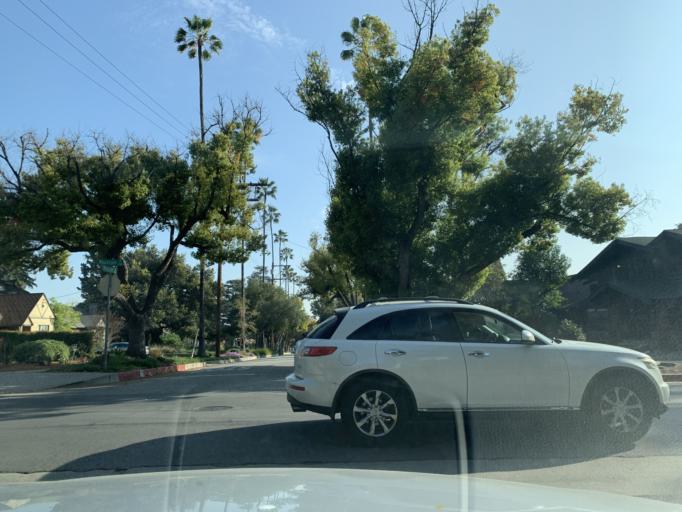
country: US
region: California
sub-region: Los Angeles County
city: Pasadena
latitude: 34.1618
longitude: -118.1231
